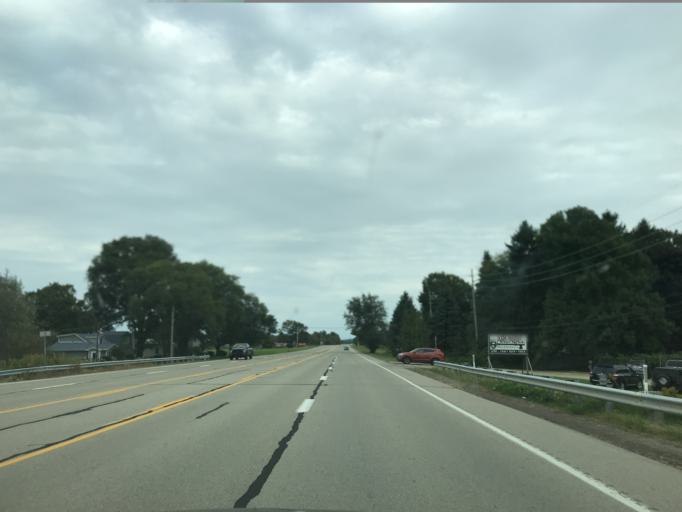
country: US
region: Pennsylvania
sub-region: Erie County
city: North East
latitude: 42.2248
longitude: -79.8057
